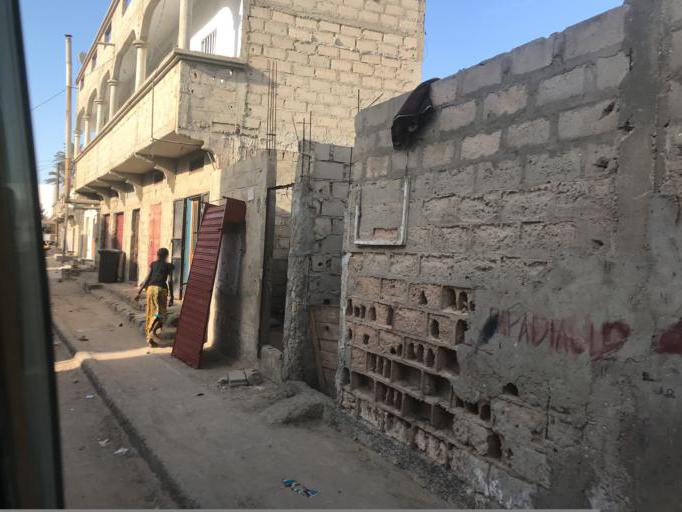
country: SN
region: Saint-Louis
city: Saint-Louis
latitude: 15.9985
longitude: -16.4953
